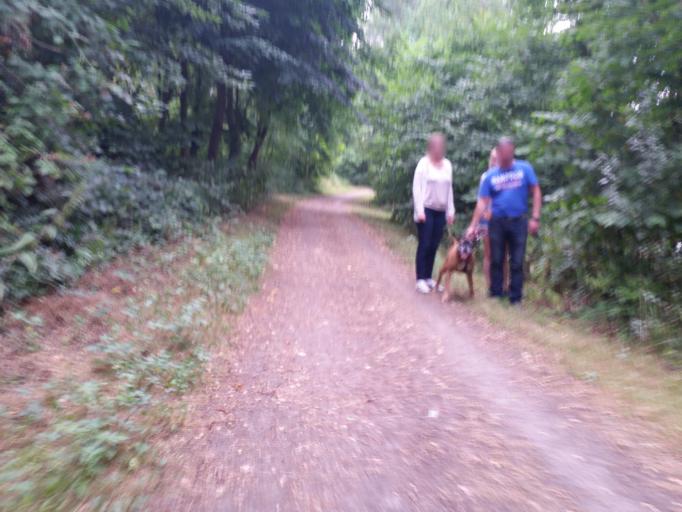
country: BE
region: Flanders
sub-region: Provincie Vlaams-Brabant
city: Zemst
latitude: 50.9769
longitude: 4.4820
